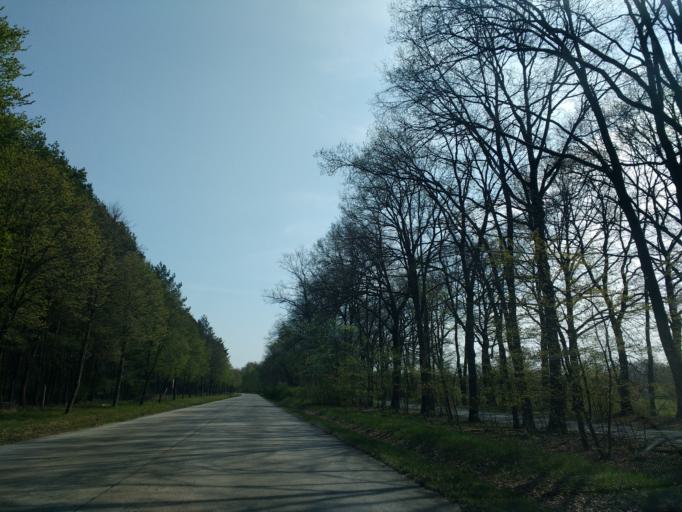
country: DE
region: North Rhine-Westphalia
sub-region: Regierungsbezirk Detmold
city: Hovelhof
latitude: 51.8251
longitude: 8.7137
